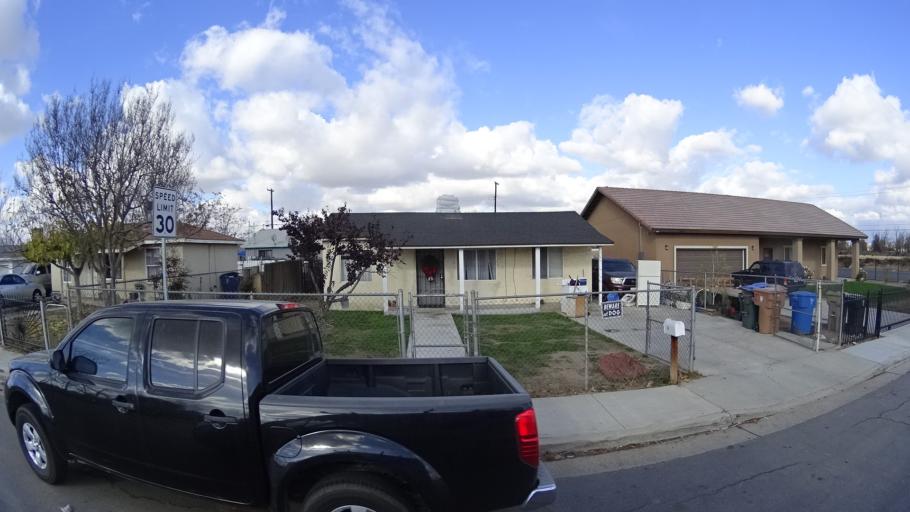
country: US
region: California
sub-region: Kern County
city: Bakersfield
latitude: 35.3321
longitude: -118.9859
